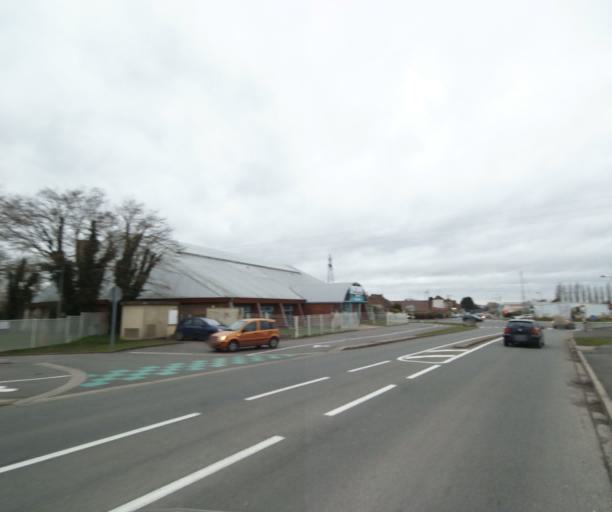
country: FR
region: Nord-Pas-de-Calais
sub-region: Departement du Nord
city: Marly
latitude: 50.3453
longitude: 3.5558
